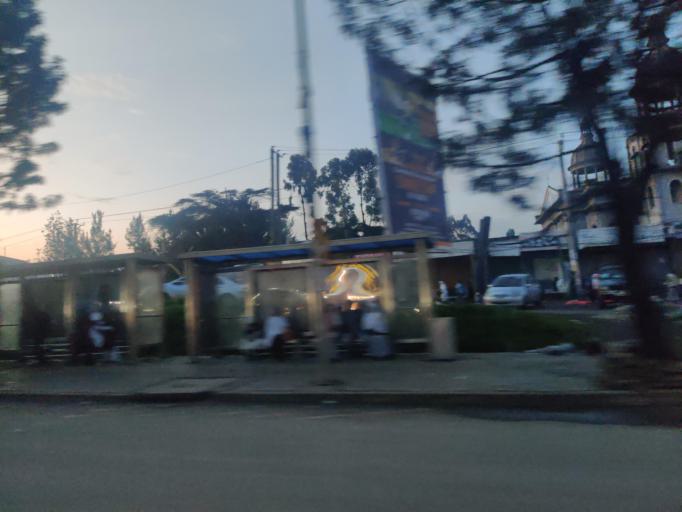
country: ET
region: Adis Abeba
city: Addis Ababa
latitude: 9.0216
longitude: 38.8403
